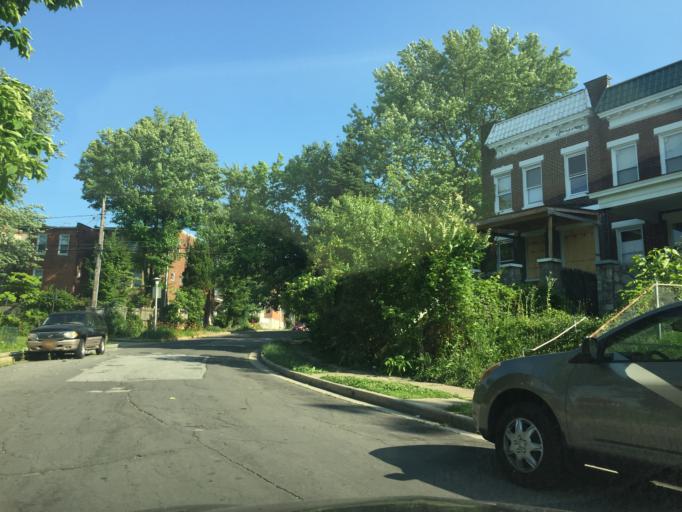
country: US
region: Maryland
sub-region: Baltimore County
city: Lochearn
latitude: 39.3393
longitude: -76.6618
